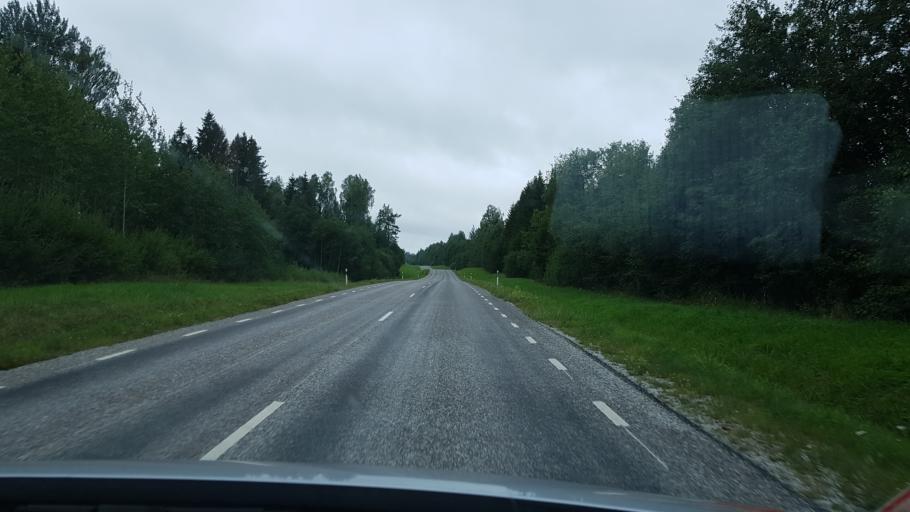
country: EE
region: Vorumaa
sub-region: Antsla vald
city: Vana-Antsla
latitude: 58.0022
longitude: 26.7079
